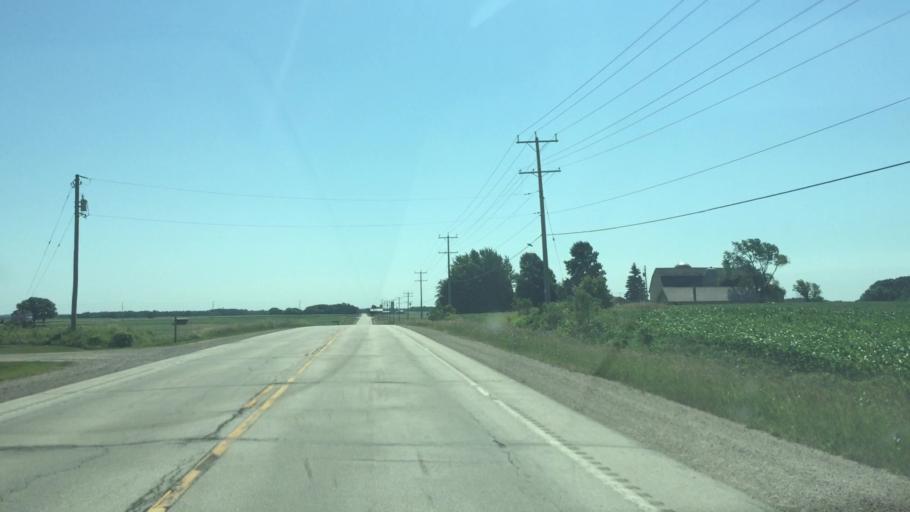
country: US
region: Wisconsin
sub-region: Calumet County
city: Hilbert
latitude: 44.1405
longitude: -88.2151
